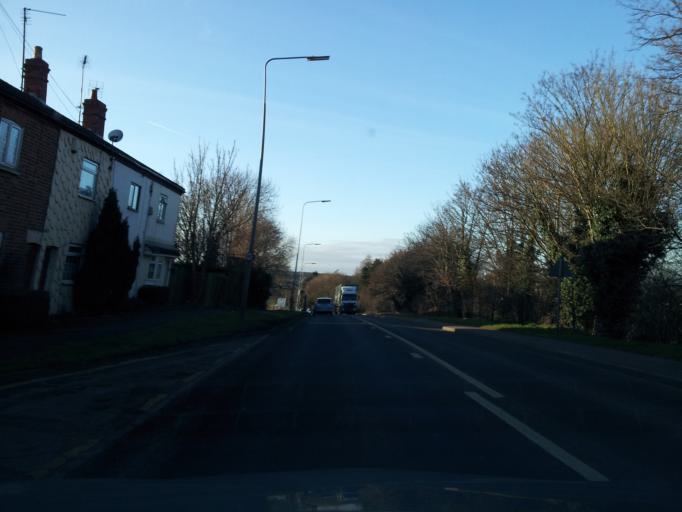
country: GB
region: England
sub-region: Northamptonshire
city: Northampton
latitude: 52.2547
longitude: -0.9389
